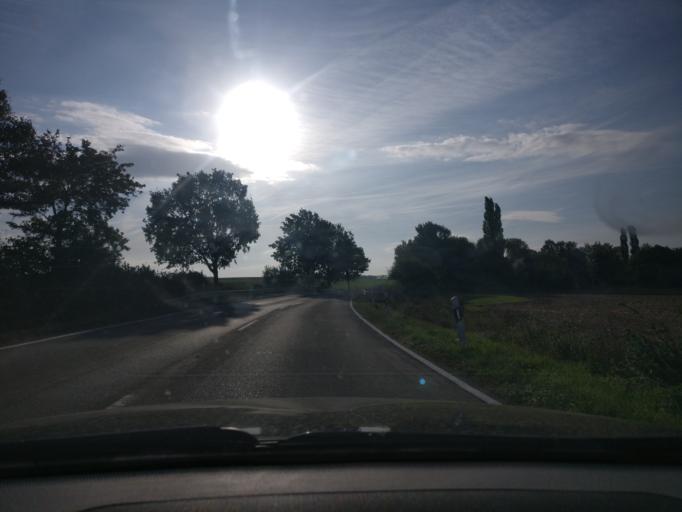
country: DE
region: Lower Saxony
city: Melle
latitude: 52.1981
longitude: 8.2584
